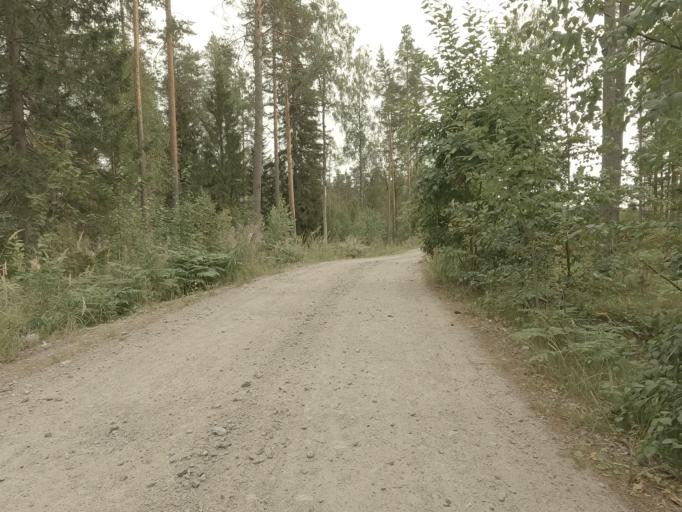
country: RU
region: Leningrad
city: Kamennogorsk
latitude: 60.9787
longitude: 29.1717
